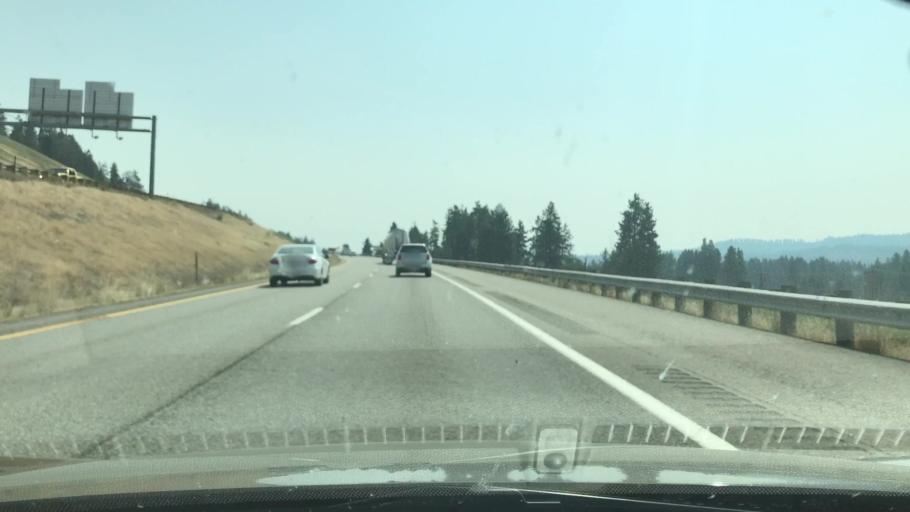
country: US
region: Idaho
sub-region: Kootenai County
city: Post Falls
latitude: 47.7098
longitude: -116.8933
